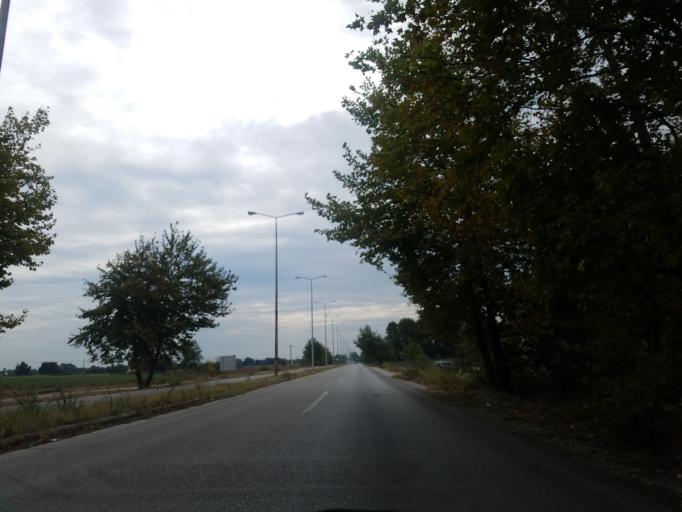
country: GR
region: Thessaly
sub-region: Trikala
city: Pyrgetos
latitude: 39.5271
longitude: 21.7473
